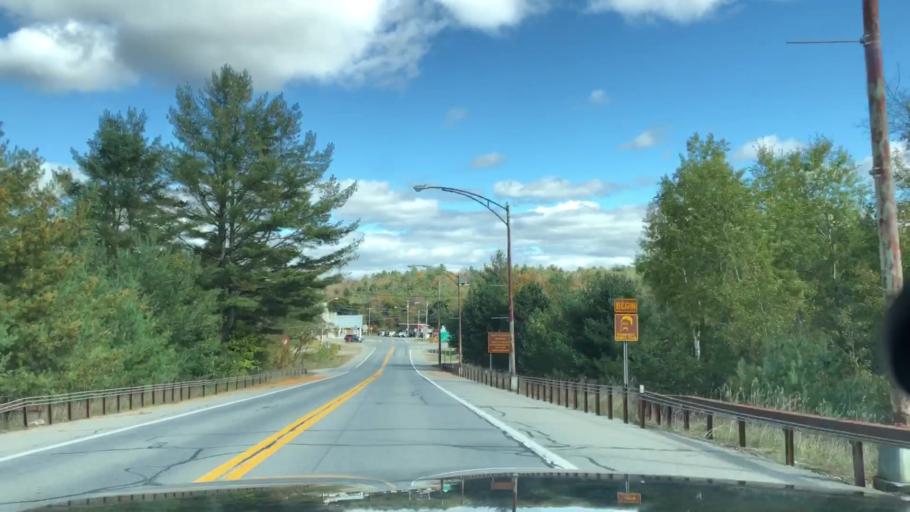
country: US
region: New York
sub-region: Warren County
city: Warrensburg
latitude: 43.6973
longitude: -73.9880
